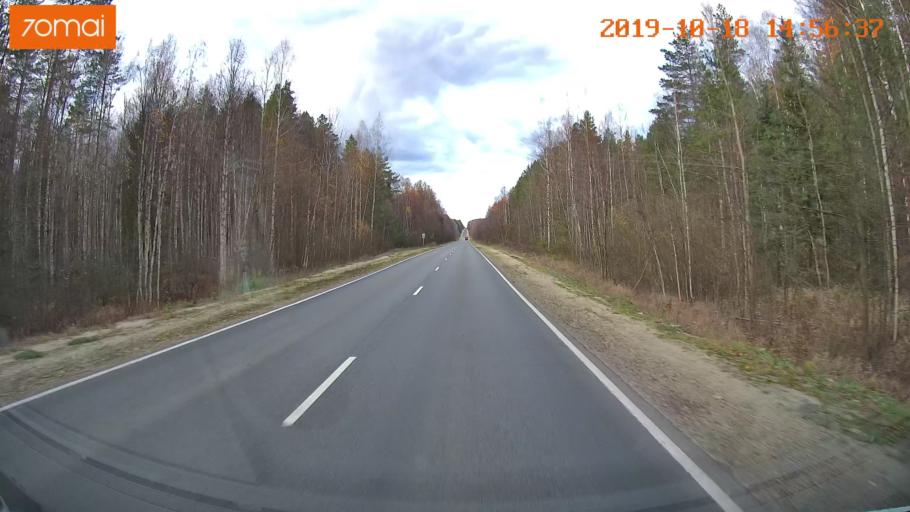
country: RU
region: Vladimir
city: Kurlovo
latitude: 55.4672
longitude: 40.5864
